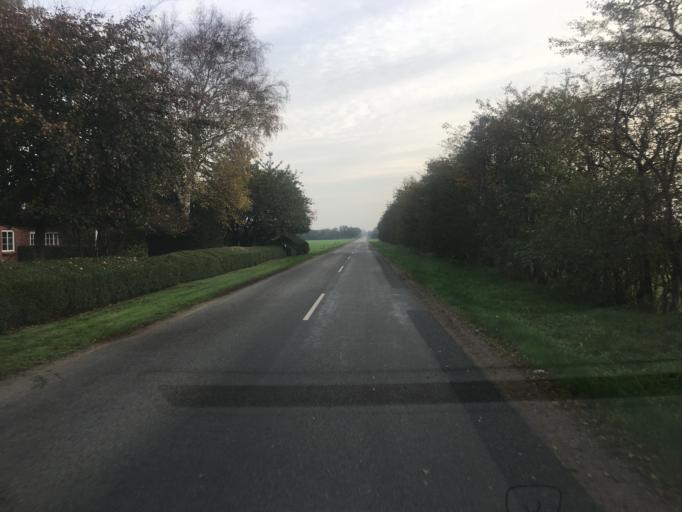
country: DK
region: South Denmark
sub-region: Tonder Kommune
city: Logumkloster
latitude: 55.0788
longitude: 9.0075
